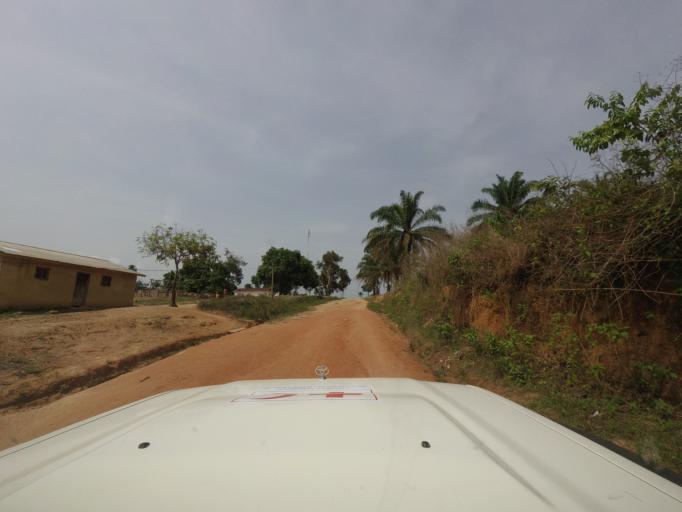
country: GN
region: Nzerekore
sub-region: Macenta
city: Macenta
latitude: 8.4547
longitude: -9.5880
